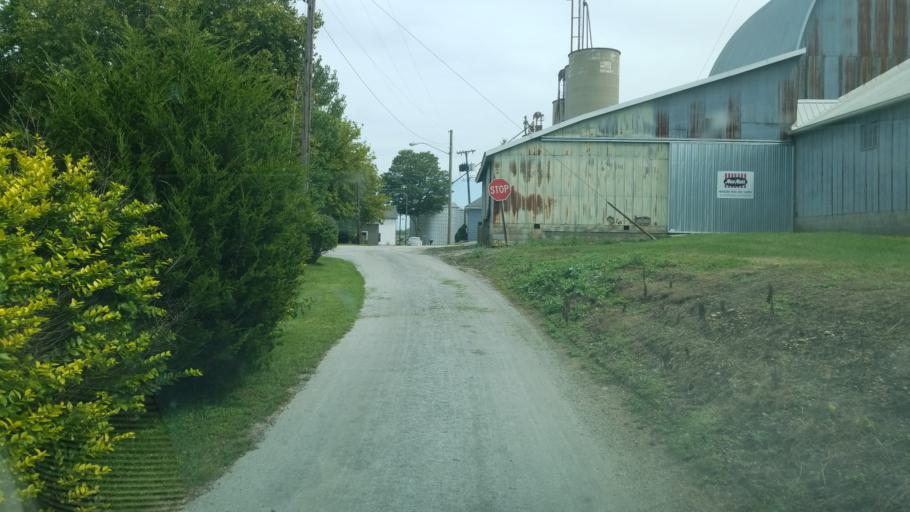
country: US
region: Ohio
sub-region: Hardin County
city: Kenton
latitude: 40.6188
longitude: -83.4686
